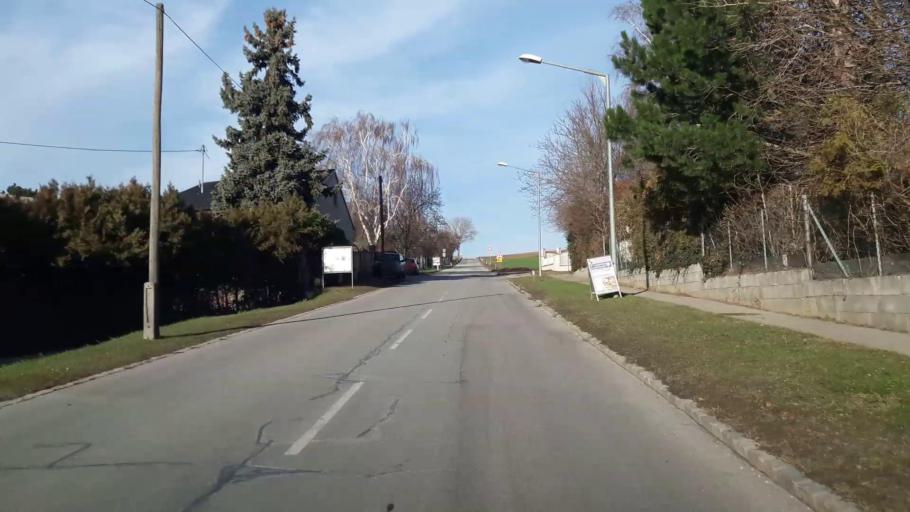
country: AT
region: Lower Austria
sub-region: Politischer Bezirk Ganserndorf
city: Auersthal
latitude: 48.3785
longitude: 16.6299
